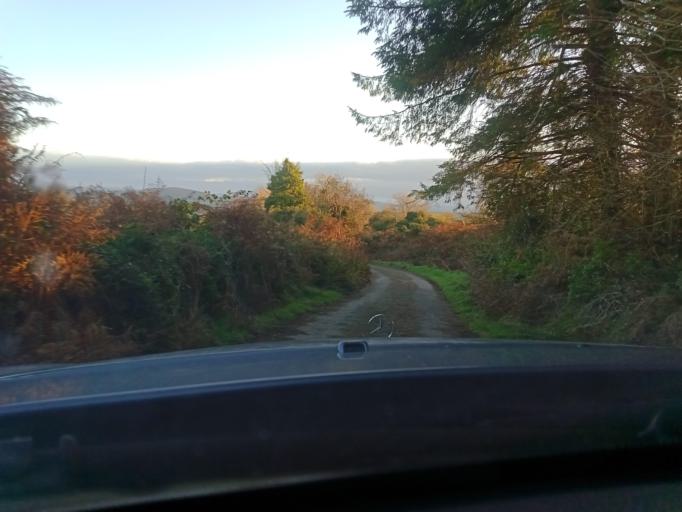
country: IE
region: Leinster
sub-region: Kilkenny
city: Graiguenamanagh
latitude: 52.4882
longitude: -6.9530
